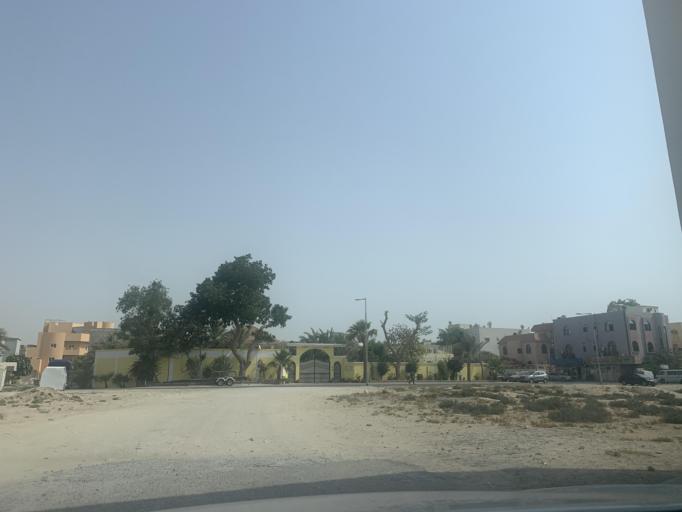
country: BH
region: Manama
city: Jidd Hafs
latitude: 26.2197
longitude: 50.4716
